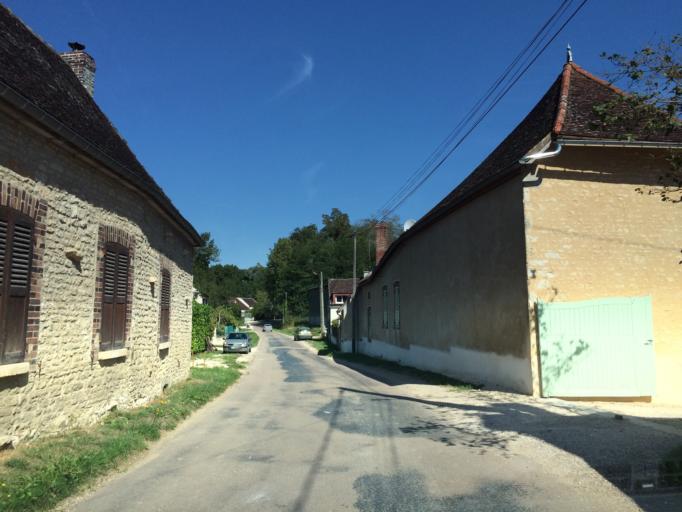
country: FR
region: Bourgogne
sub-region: Departement de l'Yonne
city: Fleury-la-Vallee
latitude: 47.8475
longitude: 3.4000
